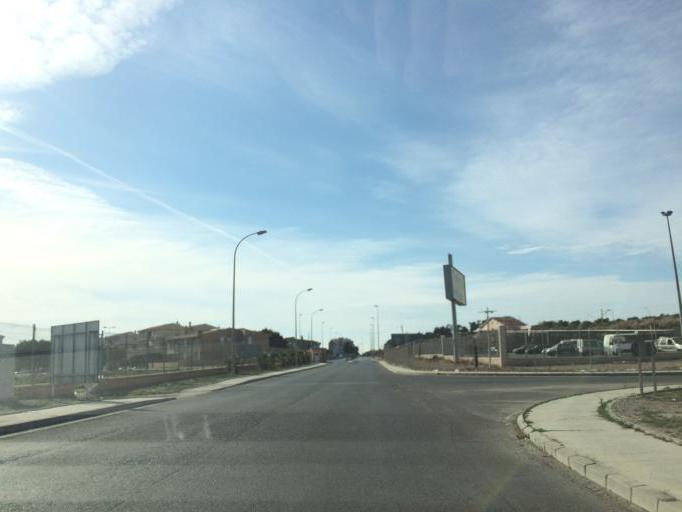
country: ES
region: Andalusia
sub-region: Provincia de Almeria
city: Almeria
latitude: 36.8519
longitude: -2.4315
